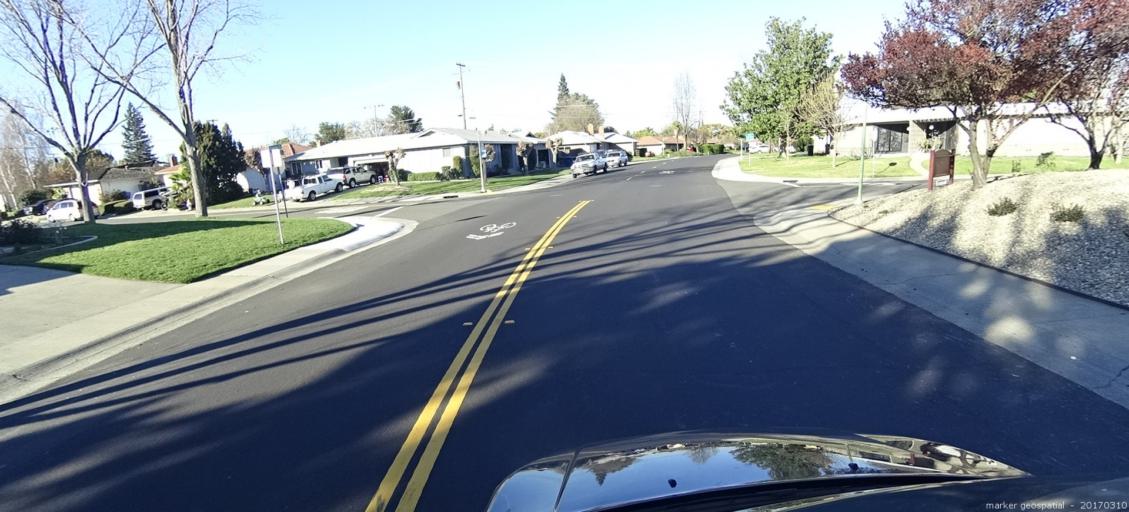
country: US
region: California
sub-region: Yolo County
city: West Sacramento
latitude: 38.5178
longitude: -121.5189
